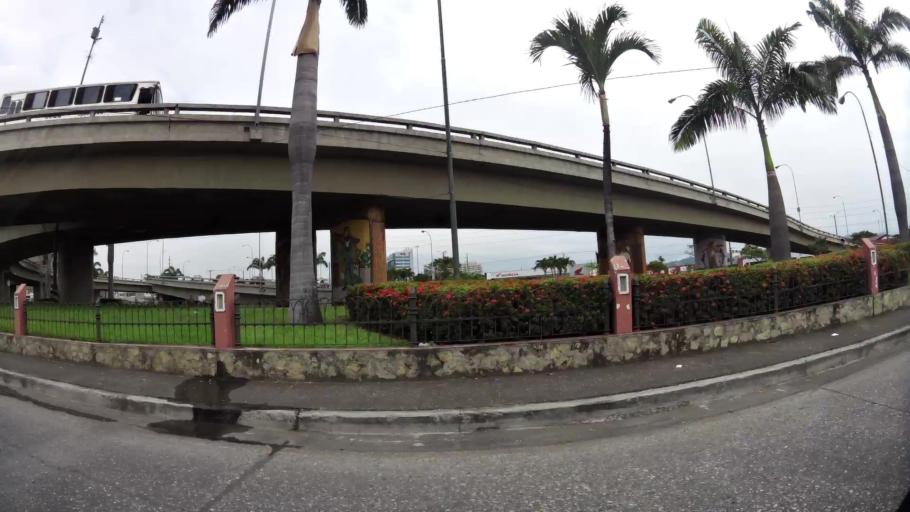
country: EC
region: Guayas
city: Eloy Alfaro
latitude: -2.1532
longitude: -79.8952
